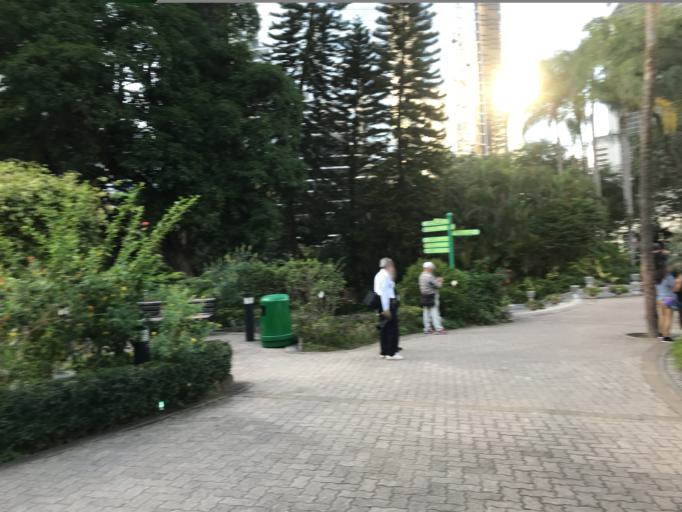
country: HK
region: Central and Western
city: Central
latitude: 22.2775
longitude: 114.1615
